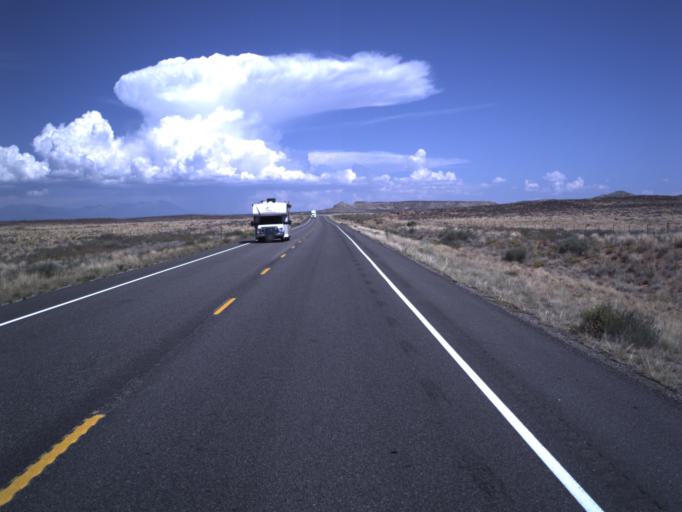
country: US
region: Utah
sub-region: San Juan County
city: Blanding
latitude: 37.3114
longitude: -109.5267
